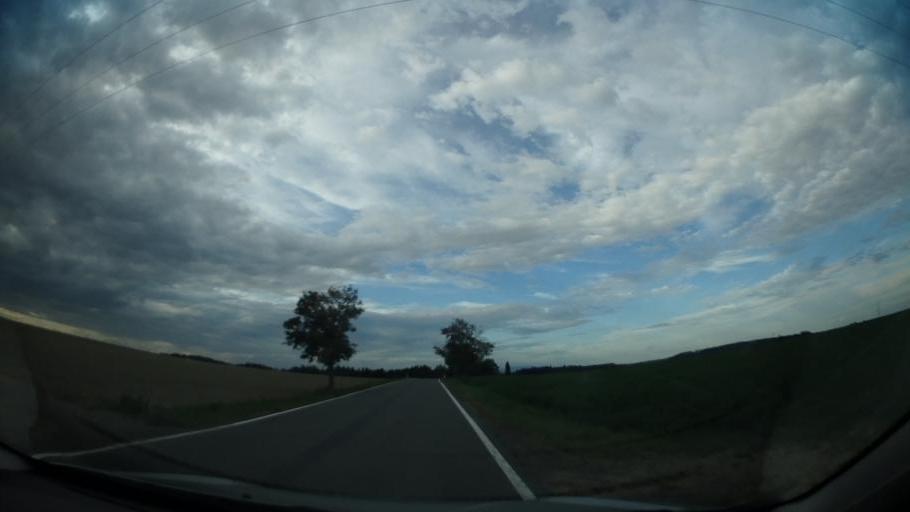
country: CZ
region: Olomoucky
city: Konice
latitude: 49.6189
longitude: 16.8929
